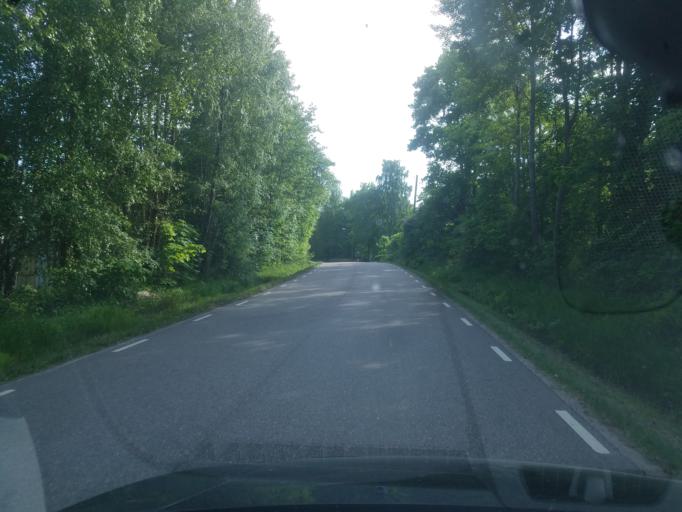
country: SE
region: Halland
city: Saro
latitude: 57.5185
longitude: 11.9506
